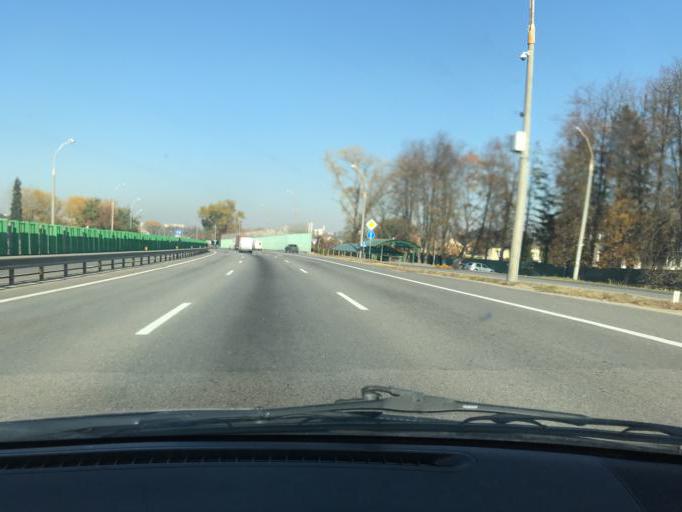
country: BY
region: Minsk
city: Syenitsa
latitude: 53.8246
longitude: 27.5339
